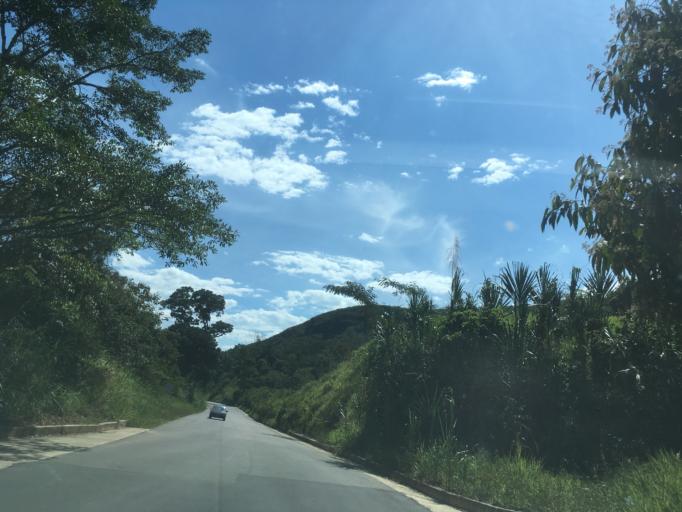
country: CO
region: Santander
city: Coromoro
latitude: 6.2991
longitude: -73.1463
